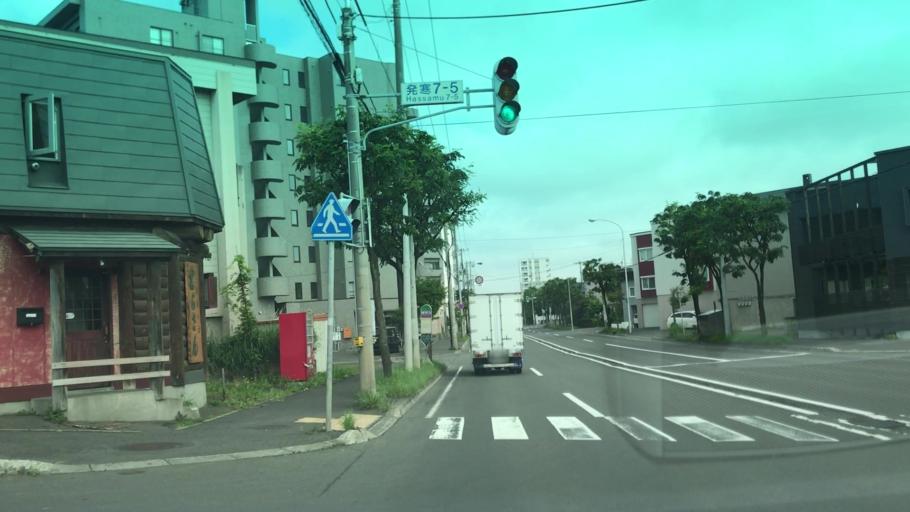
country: JP
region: Hokkaido
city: Sapporo
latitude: 43.0900
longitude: 141.2894
